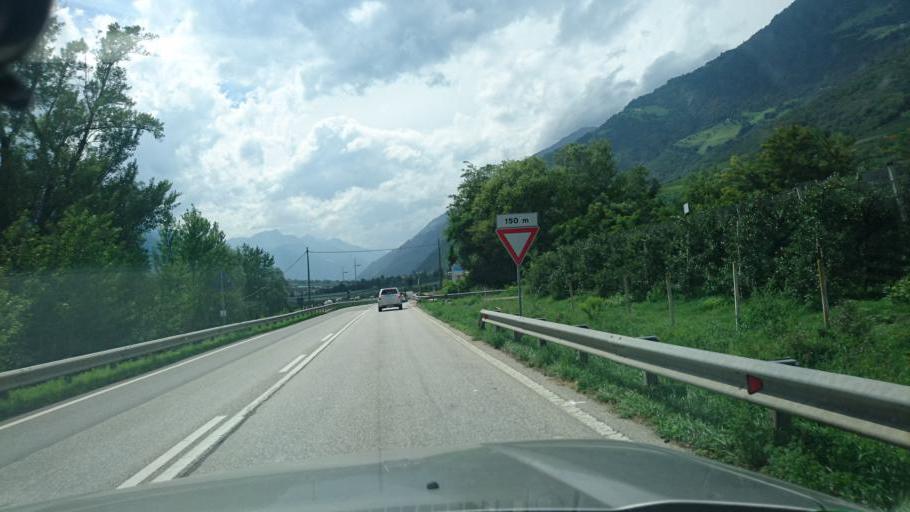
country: IT
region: Trentino-Alto Adige
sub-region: Bolzano
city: Naturno
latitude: 46.6534
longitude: 11.0197
